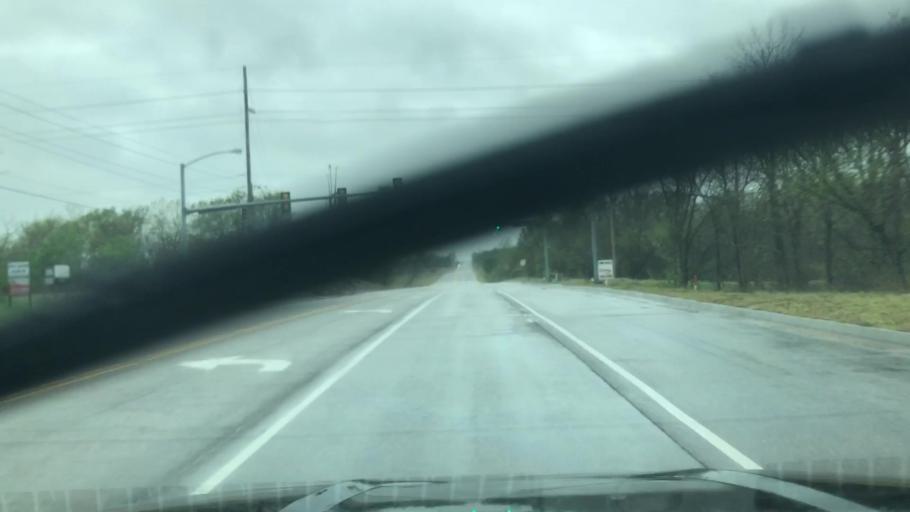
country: US
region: Oklahoma
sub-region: Tulsa County
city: Owasso
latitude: 36.2641
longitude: -95.9012
